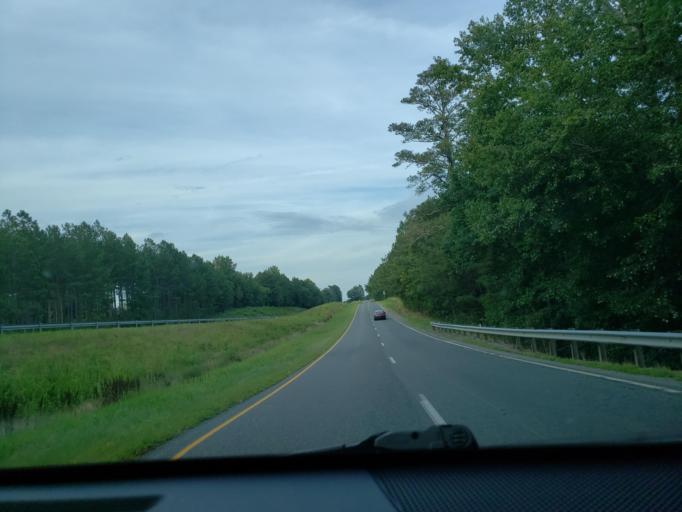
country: US
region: Virginia
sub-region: Brunswick County
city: Lawrenceville
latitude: 36.7432
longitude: -77.8870
